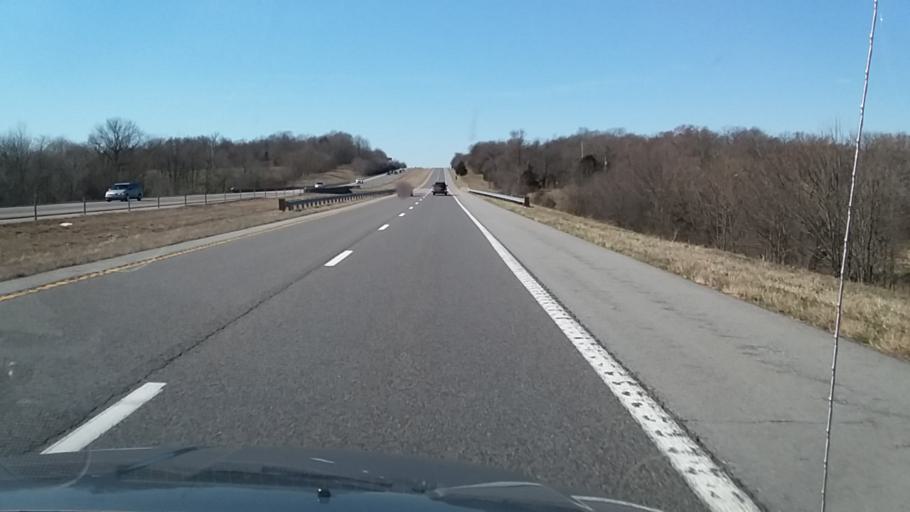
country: US
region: Missouri
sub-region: Cape Girardeau County
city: Jackson
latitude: 37.5341
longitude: -89.7172
